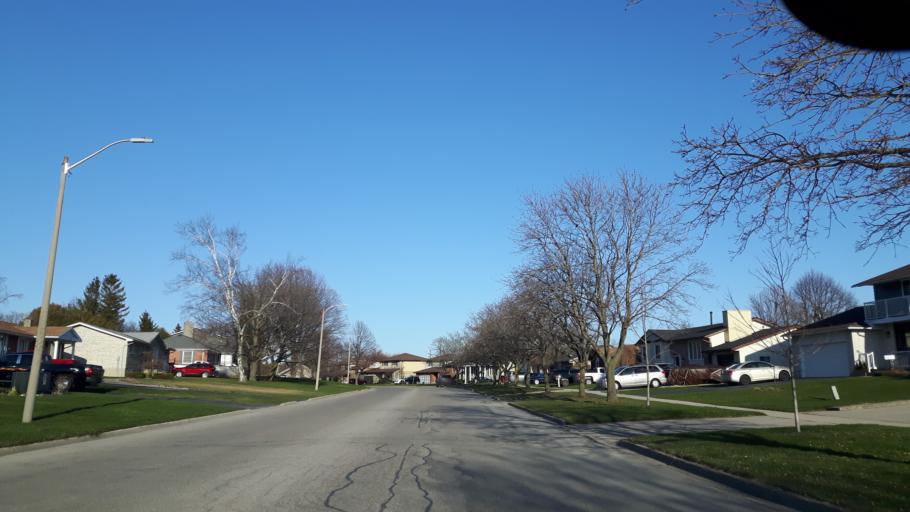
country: CA
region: Ontario
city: Goderich
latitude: 43.7298
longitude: -81.7131
